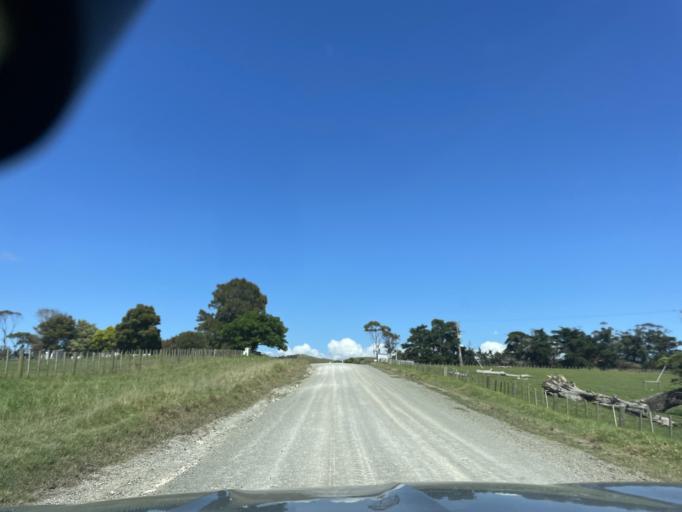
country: NZ
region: Auckland
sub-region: Auckland
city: Wellsford
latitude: -36.2875
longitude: 174.3388
